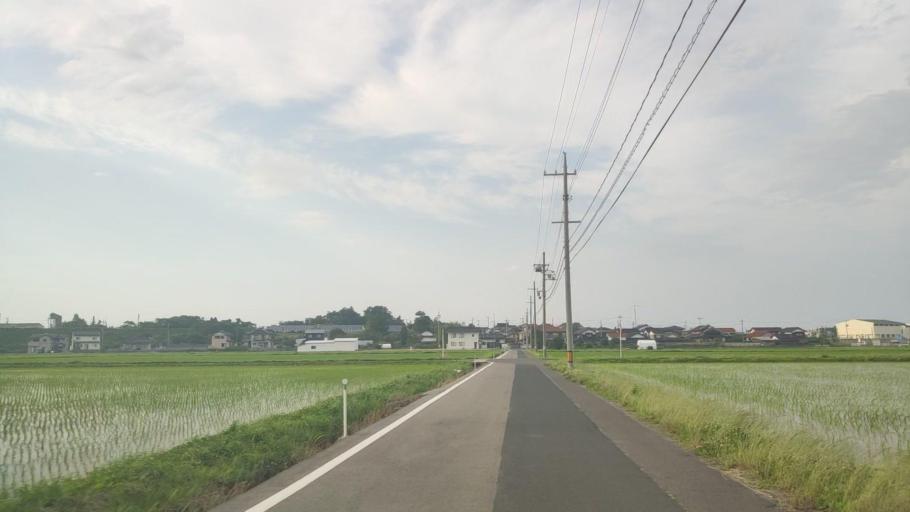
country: JP
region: Tottori
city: Kurayoshi
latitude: 35.4854
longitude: 133.8134
